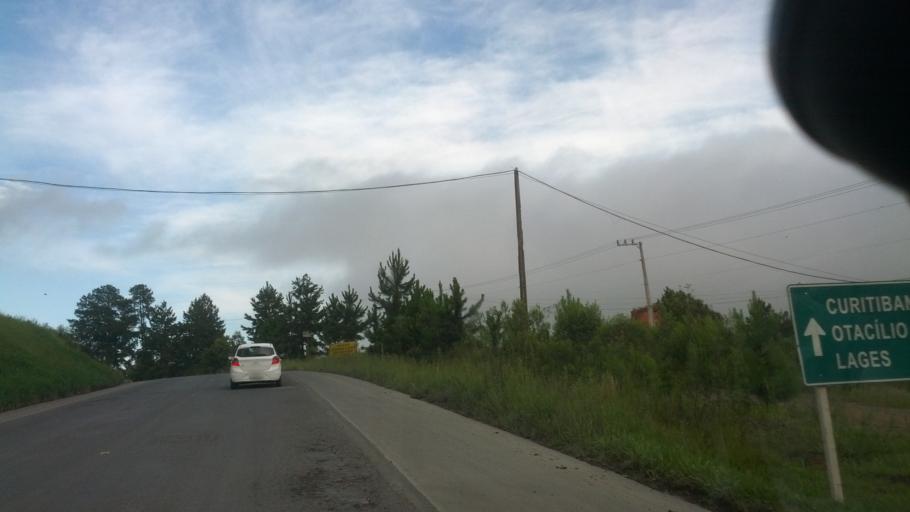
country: BR
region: Santa Catarina
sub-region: Otacilio Costa
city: Otacilio Costa
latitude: -27.2498
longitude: -49.9613
